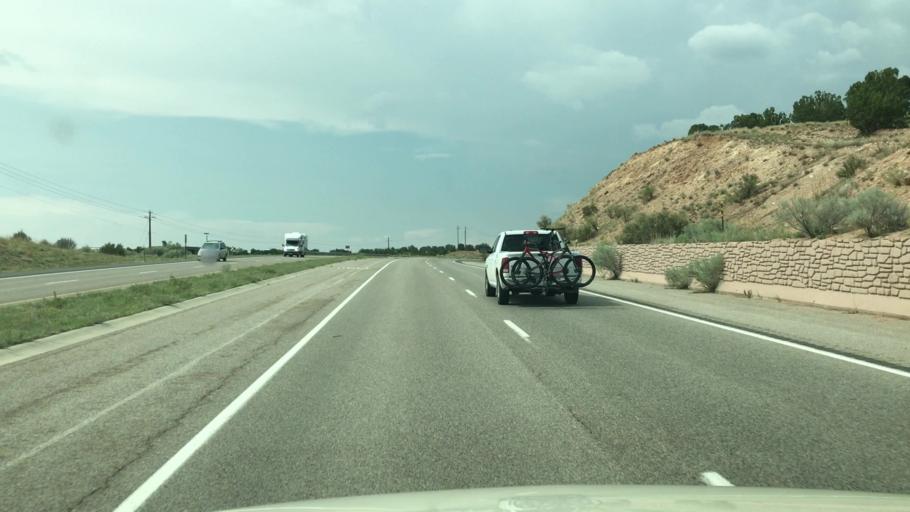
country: US
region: New Mexico
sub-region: Santa Fe County
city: Eldorado at Santa Fe
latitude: 35.4908
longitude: -105.9026
